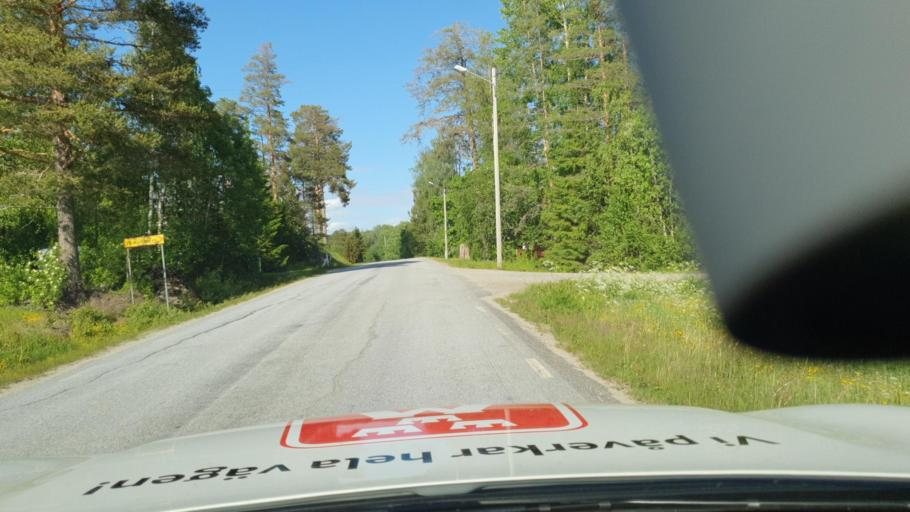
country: SE
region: Vaesterbotten
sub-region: Vannas Kommun
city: Vaennaes
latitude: 63.8610
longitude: 19.6407
